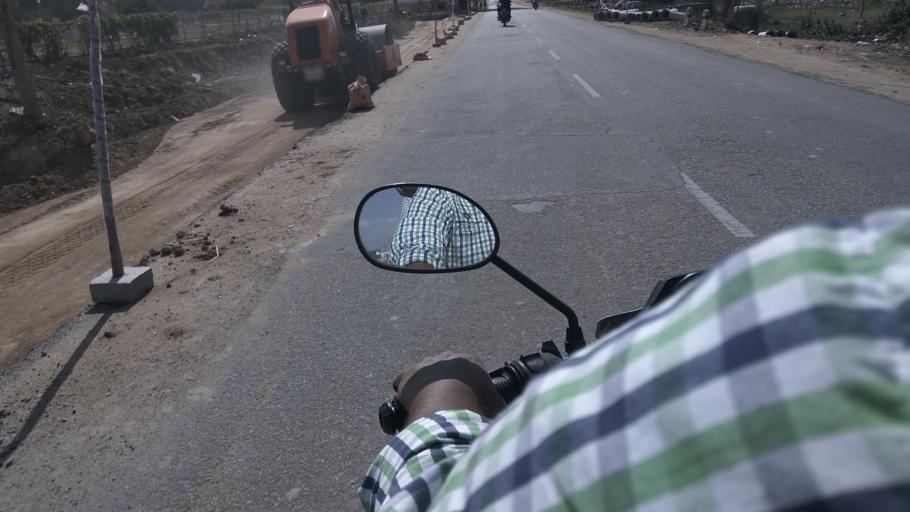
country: IN
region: Karnataka
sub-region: Kolar
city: Mulbagal
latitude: 13.1604
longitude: 78.3830
